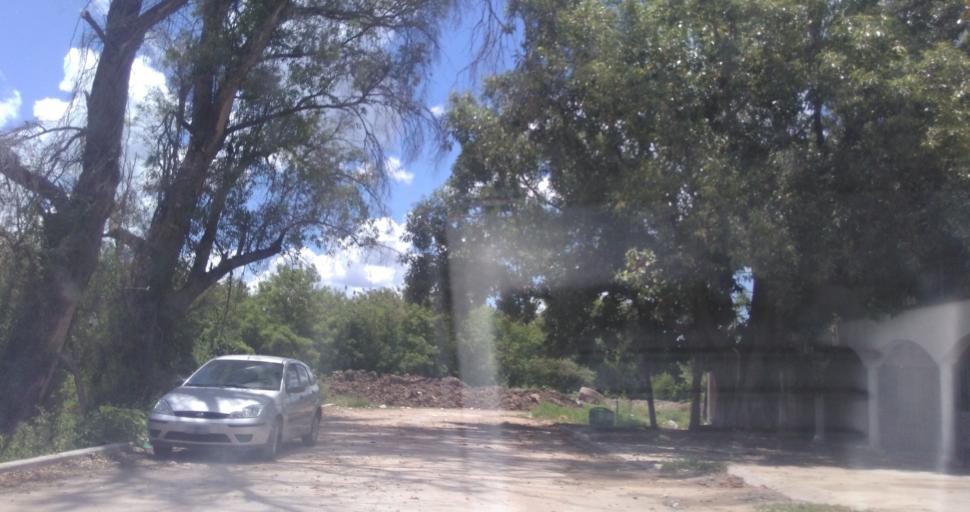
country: AR
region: Chaco
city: Resistencia
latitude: -27.4363
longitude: -58.9728
